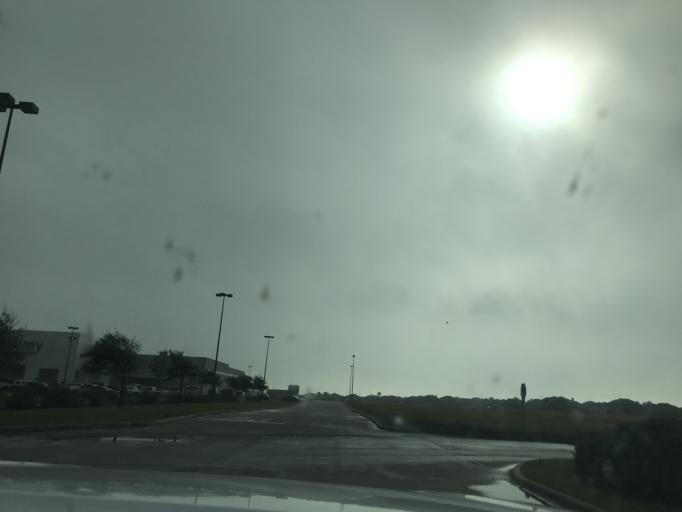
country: US
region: Texas
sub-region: San Patricio County
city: Portland
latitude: 27.8932
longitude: -97.3086
